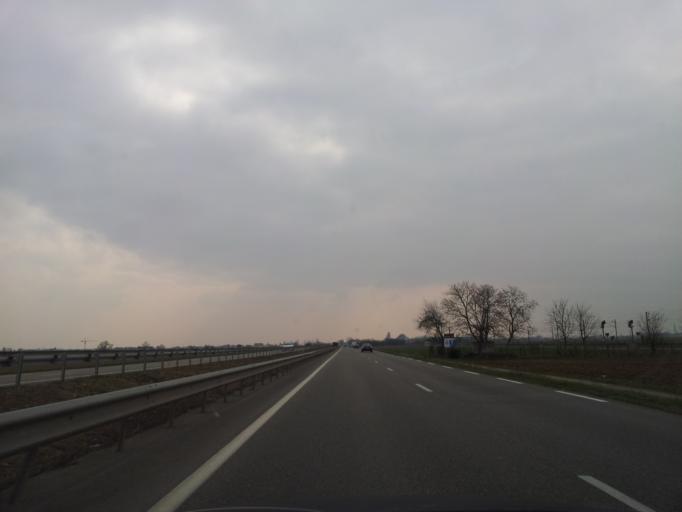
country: FR
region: Alsace
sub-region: Departement du Bas-Rhin
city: Erstein
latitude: 48.4392
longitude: 7.6494
